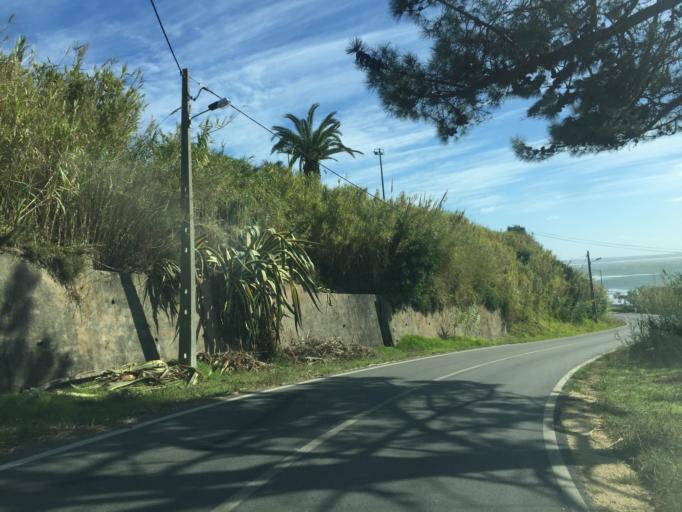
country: PT
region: Coimbra
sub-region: Figueira da Foz
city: Buarcos
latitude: 40.1783
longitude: -8.9003
